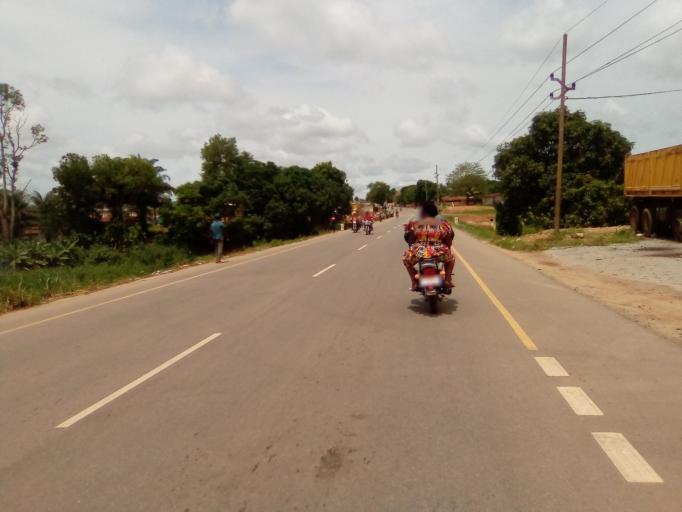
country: SL
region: Southern Province
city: Bo
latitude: 7.9371
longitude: -11.7258
